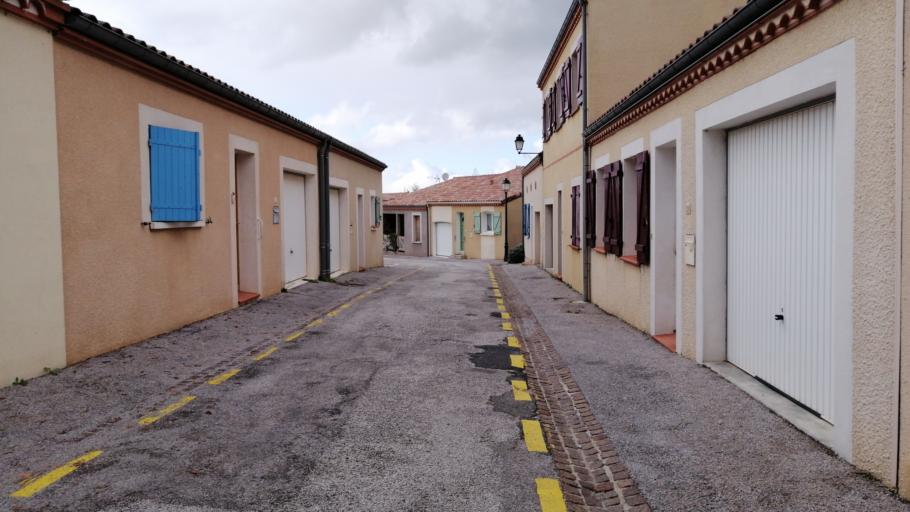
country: FR
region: Midi-Pyrenees
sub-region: Departement du Tarn
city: Soreze
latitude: 43.4539
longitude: 2.0702
